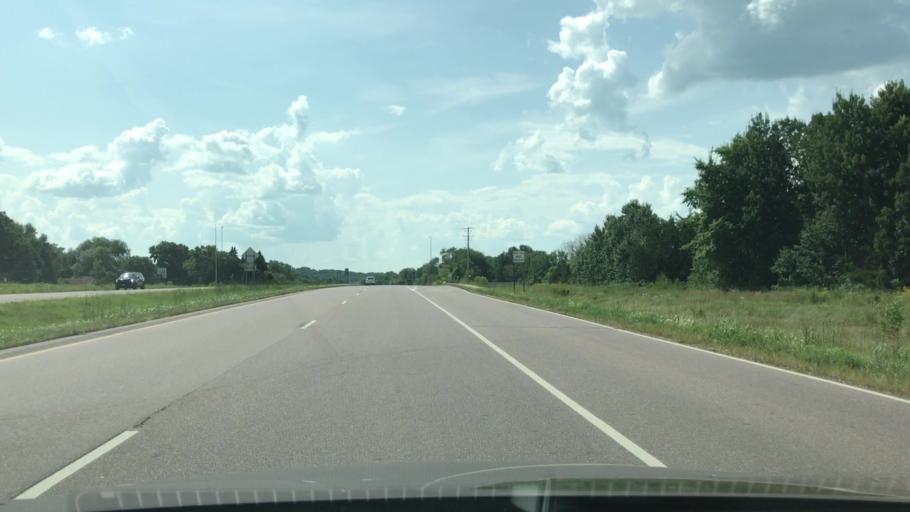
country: US
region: Minnesota
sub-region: Nicollet County
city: North Mankato
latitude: 44.1525
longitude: -94.0605
